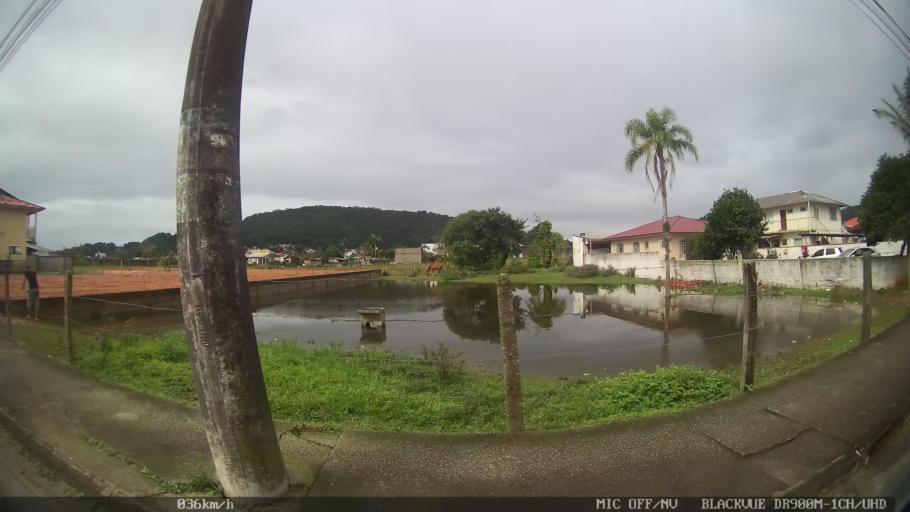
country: BR
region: Santa Catarina
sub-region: Biguacu
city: Biguacu
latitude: -27.5178
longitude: -48.6561
